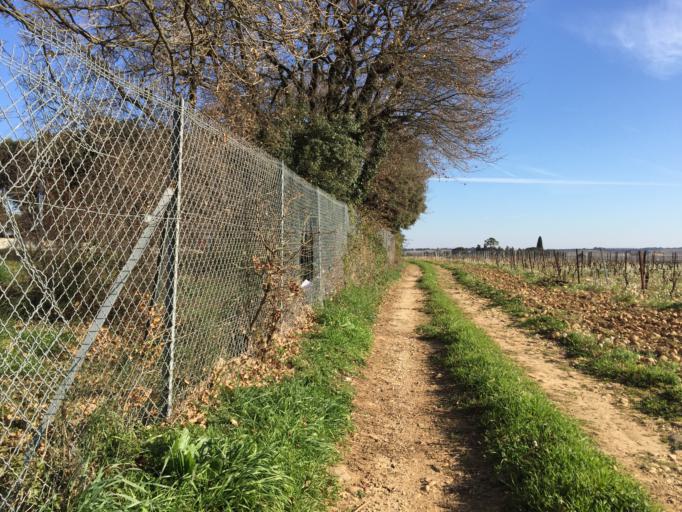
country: FR
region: Provence-Alpes-Cote d'Azur
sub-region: Departement du Vaucluse
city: Orange
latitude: 44.1113
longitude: 4.8286
